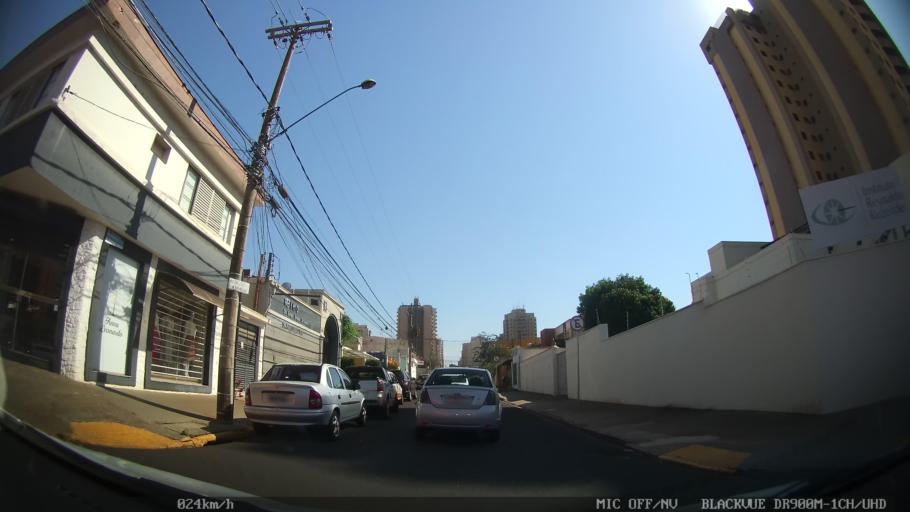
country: BR
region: Sao Paulo
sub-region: Ribeirao Preto
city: Ribeirao Preto
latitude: -21.1874
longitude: -47.8040
